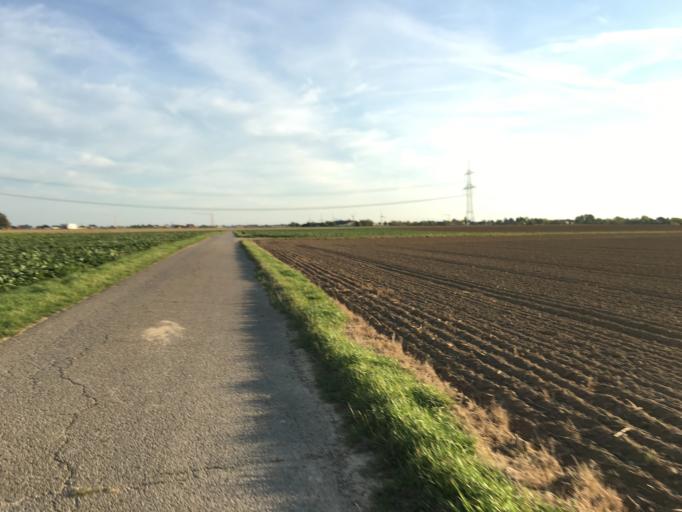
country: DE
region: North Rhine-Westphalia
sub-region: Regierungsbezirk Koln
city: Merzenich
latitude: 50.8429
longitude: 6.5332
